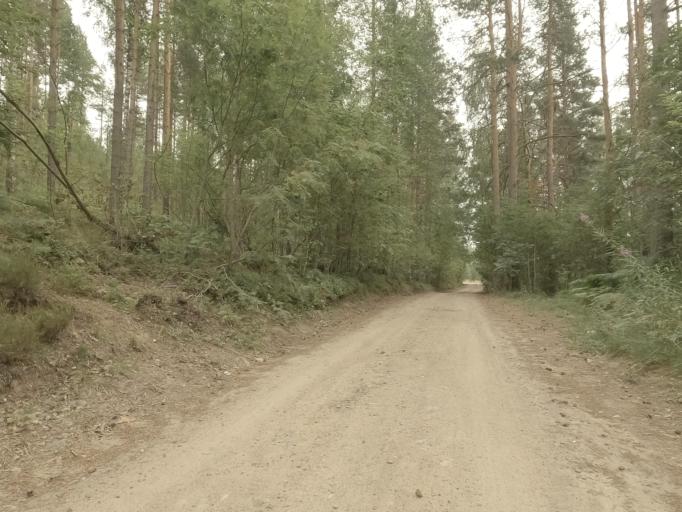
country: RU
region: Leningrad
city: Kamennogorsk
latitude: 60.9961
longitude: 29.1839
